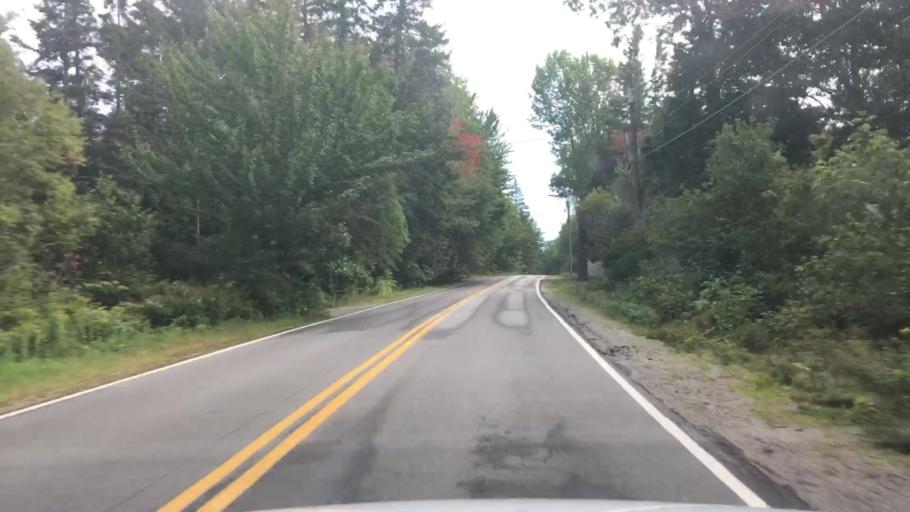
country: US
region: Maine
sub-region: Hancock County
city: Trenton
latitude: 44.4609
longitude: -68.4243
